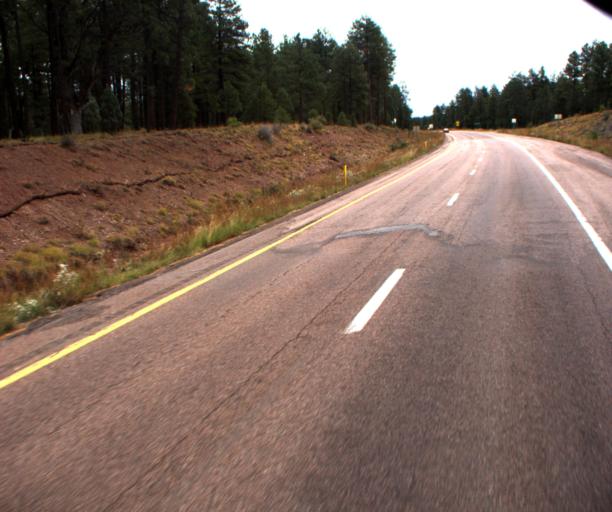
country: US
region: Arizona
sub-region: Gila County
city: Star Valley
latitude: 34.2975
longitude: -110.9865
